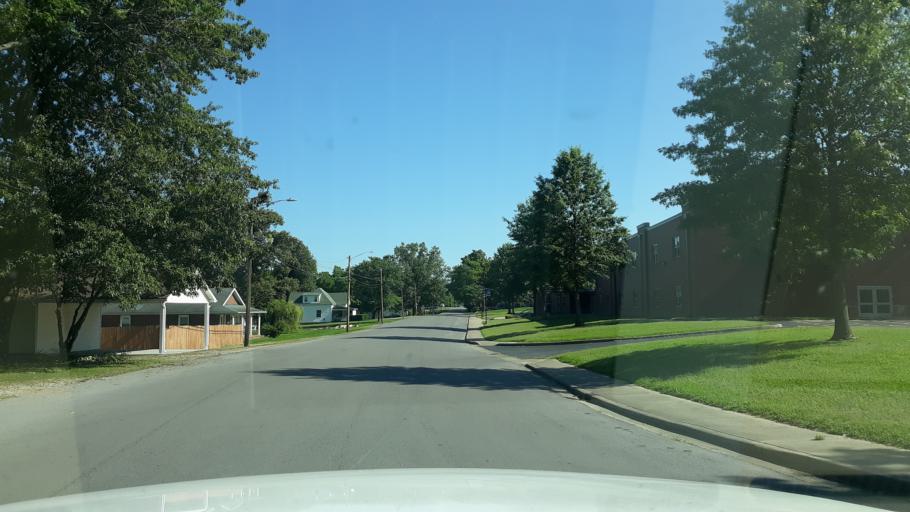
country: US
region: Illinois
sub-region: Saline County
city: Eldorado
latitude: 37.8198
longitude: -88.4362
